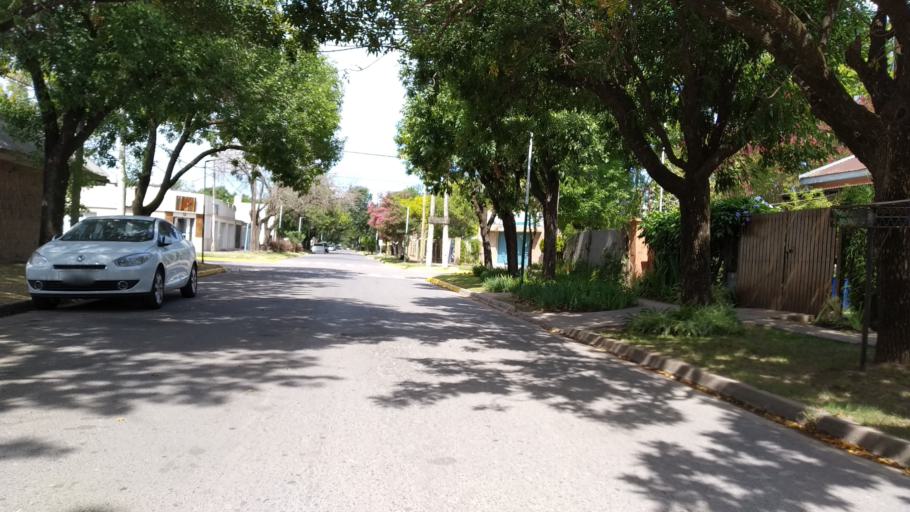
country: AR
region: Santa Fe
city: Funes
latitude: -32.9189
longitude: -60.8134
